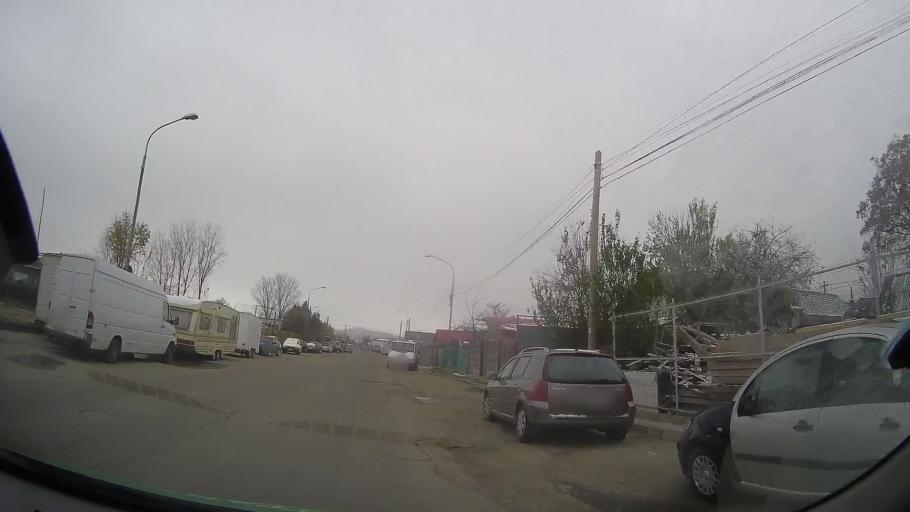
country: RO
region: Vaslui
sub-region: Municipiul Barlad
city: Barlad
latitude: 46.2381
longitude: 27.6780
